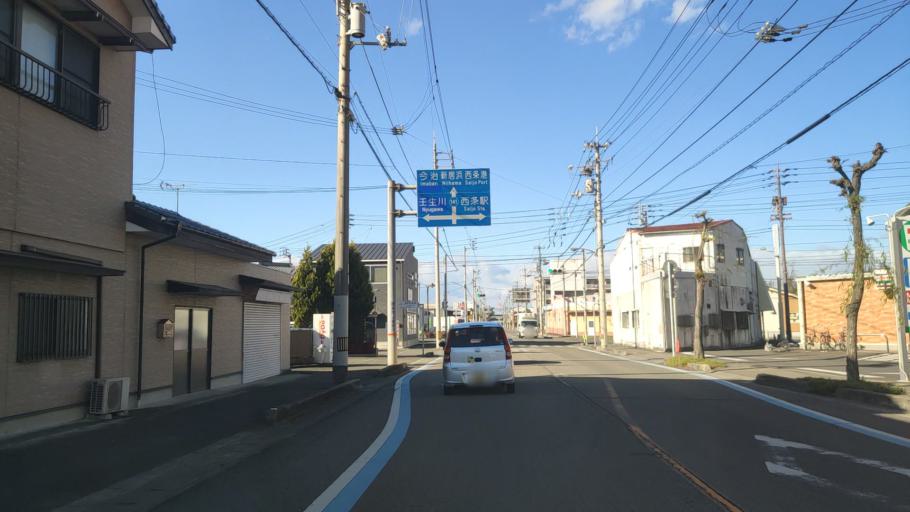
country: JP
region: Ehime
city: Saijo
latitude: 33.9111
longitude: 133.1806
